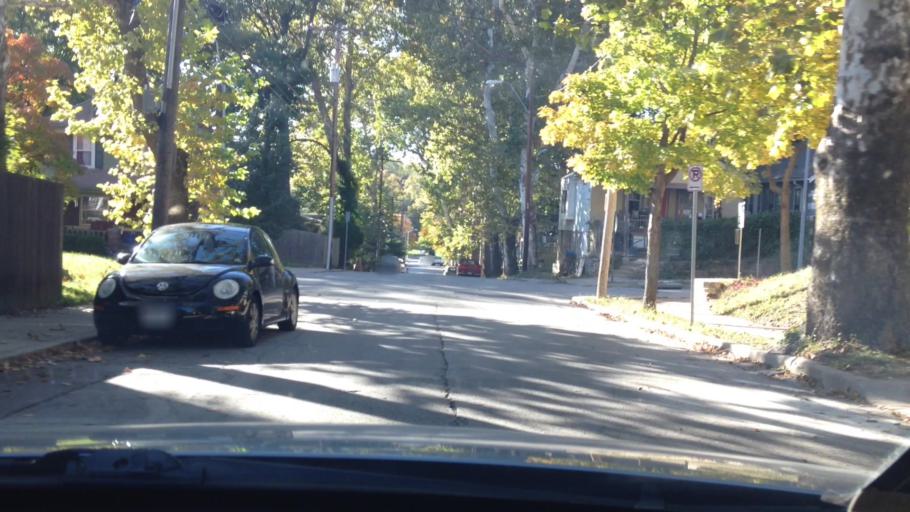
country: US
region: Kansas
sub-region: Johnson County
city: Westwood
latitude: 39.0490
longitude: -94.5757
